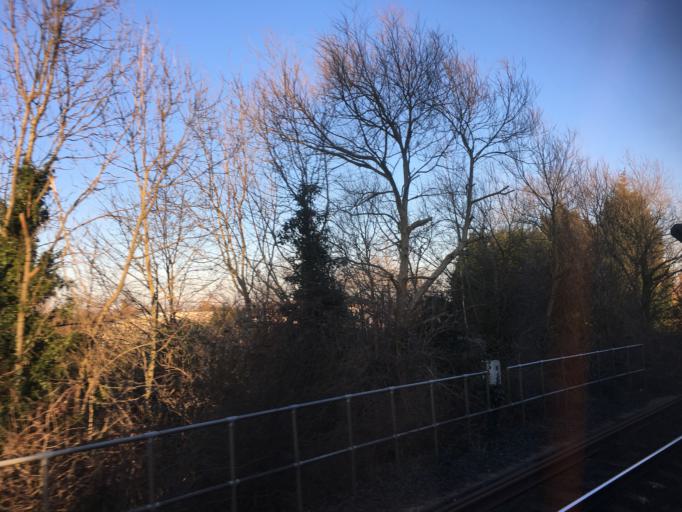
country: GB
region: England
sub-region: Derbyshire
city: Long Eaton
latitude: 52.8843
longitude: -1.2798
